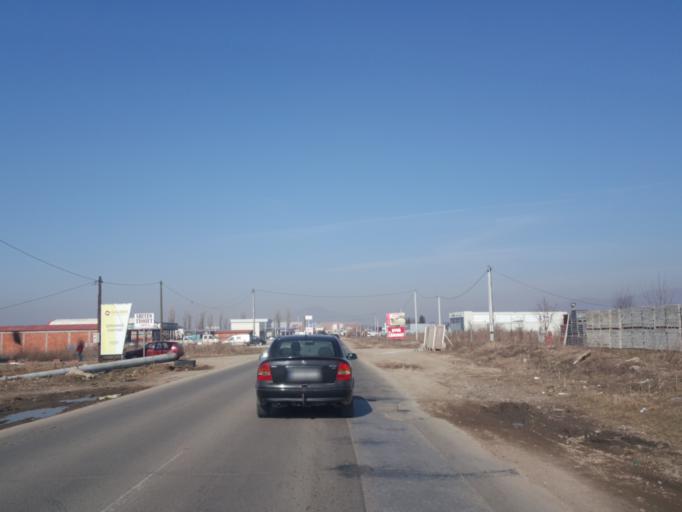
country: XK
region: Mitrovica
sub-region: Vushtrri
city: Vushtrri
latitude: 42.8060
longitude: 20.9906
